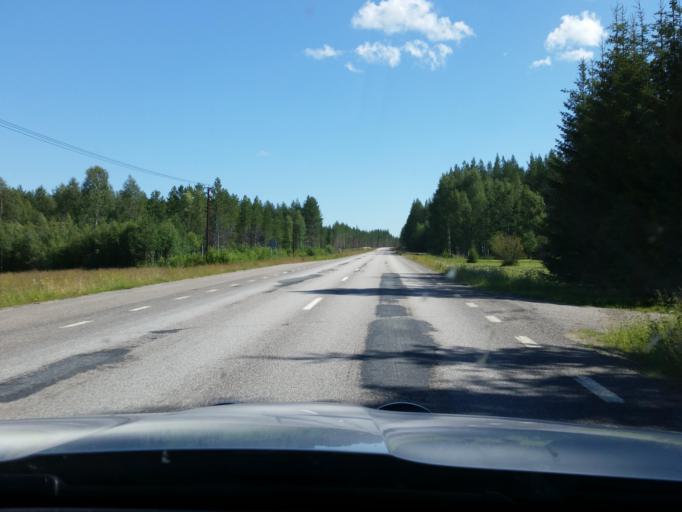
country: SE
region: Norrbotten
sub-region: Alvsbyns Kommun
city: AElvsbyn
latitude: 65.6881
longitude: 20.7004
